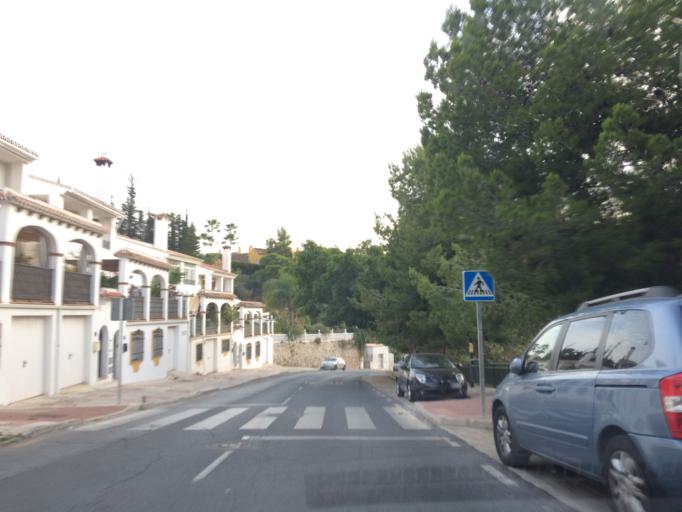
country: ES
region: Andalusia
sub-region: Provincia de Malaga
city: Malaga
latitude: 36.7325
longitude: -4.3942
